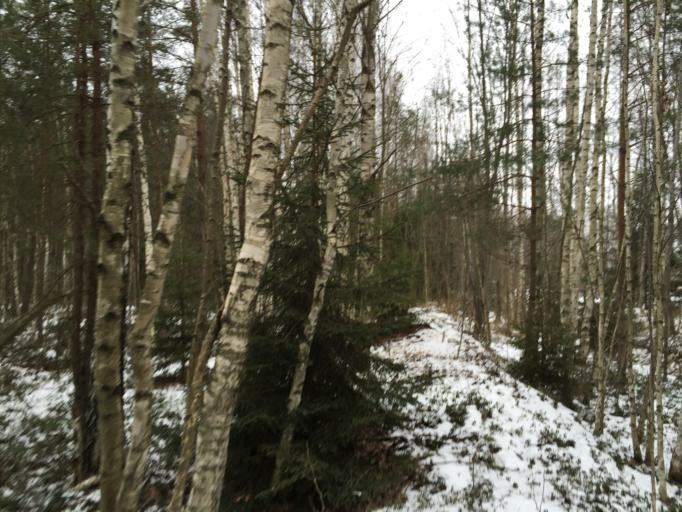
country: LV
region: Saulkrastu
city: Saulkrasti
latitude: 57.2380
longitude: 24.5058
